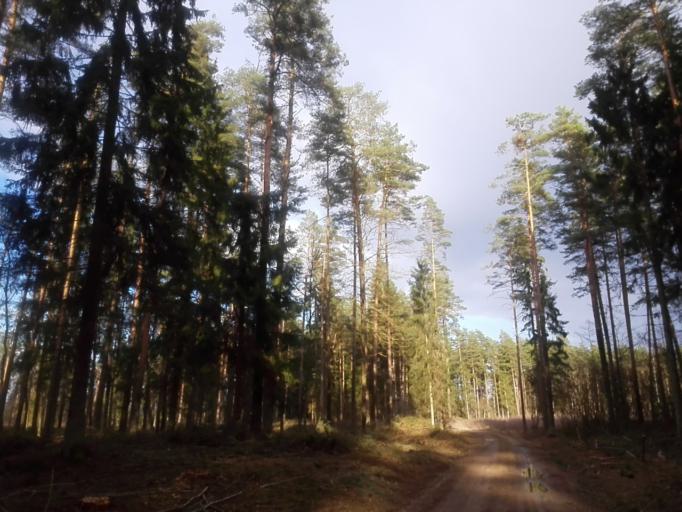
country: PL
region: Podlasie
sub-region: Powiat sejnenski
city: Sejny
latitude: 54.0309
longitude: 23.3846
